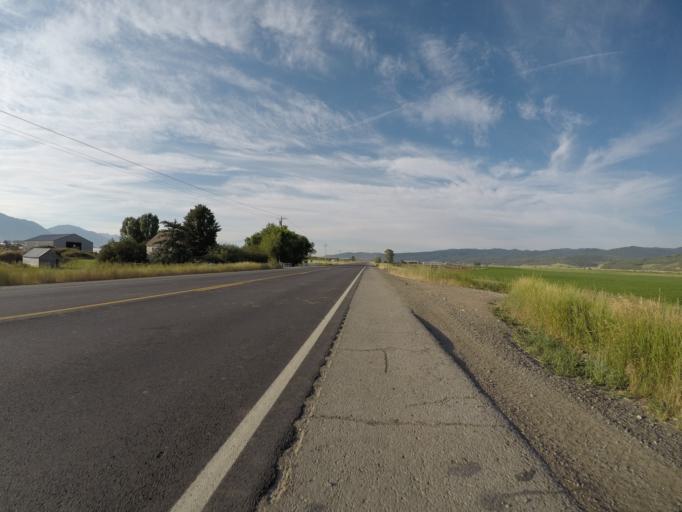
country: US
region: Wyoming
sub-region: Lincoln County
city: Afton
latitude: 42.9647
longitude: -111.0124
